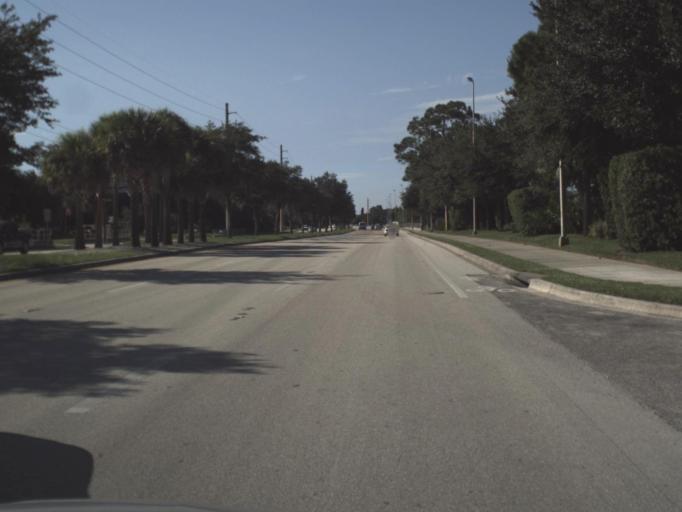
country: US
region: Florida
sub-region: Sarasota County
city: South Venice
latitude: 27.0225
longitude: -82.3922
